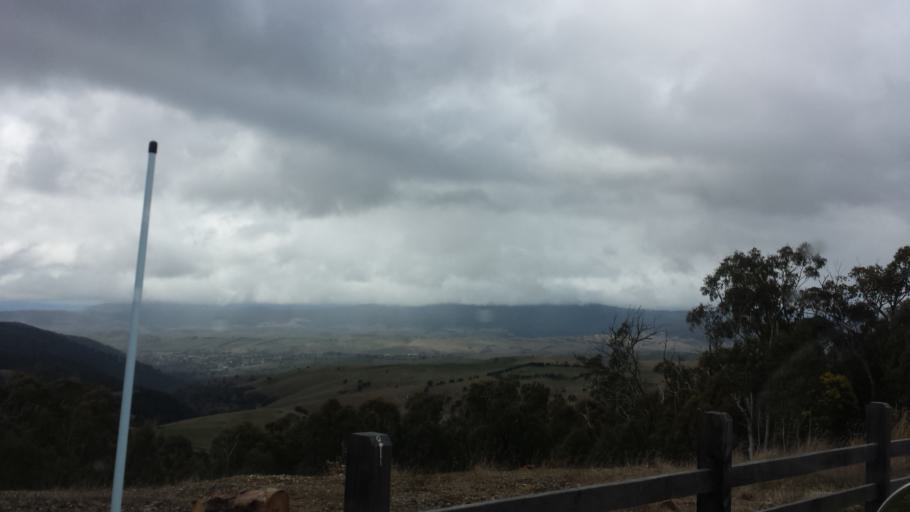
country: AU
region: Victoria
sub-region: Alpine
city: Mount Beauty
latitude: -37.1266
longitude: 147.5344
